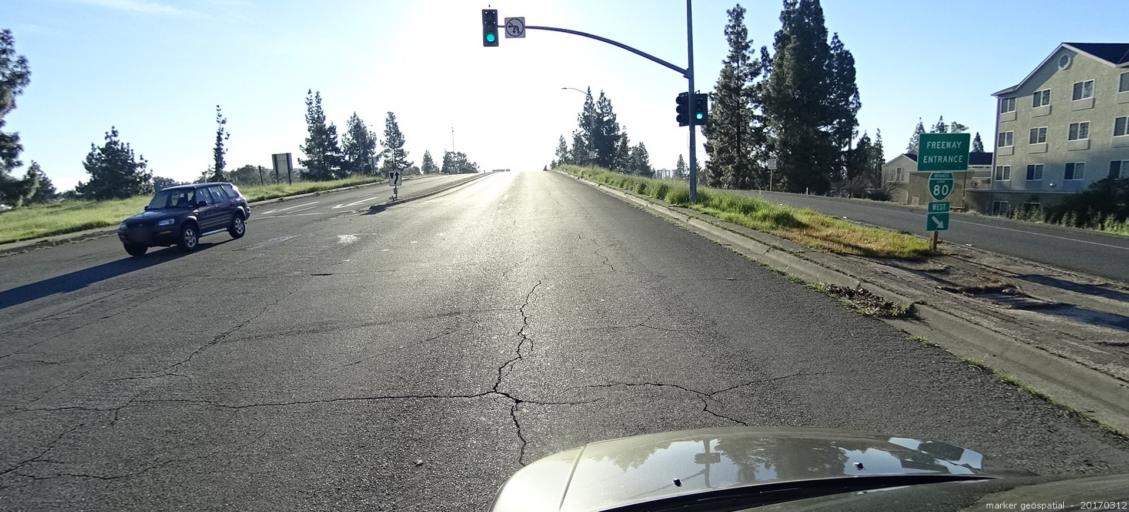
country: US
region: California
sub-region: Sacramento County
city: Sacramento
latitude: 38.5975
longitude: -121.4457
